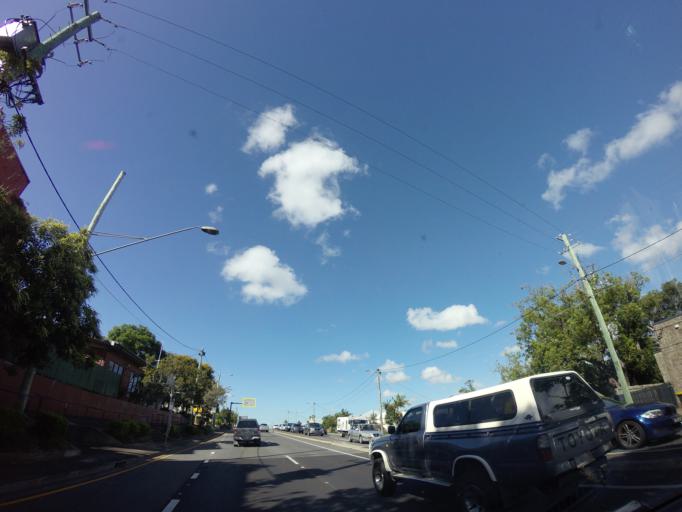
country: AU
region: Queensland
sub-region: Brisbane
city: Annerley
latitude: -27.5093
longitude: 153.0331
